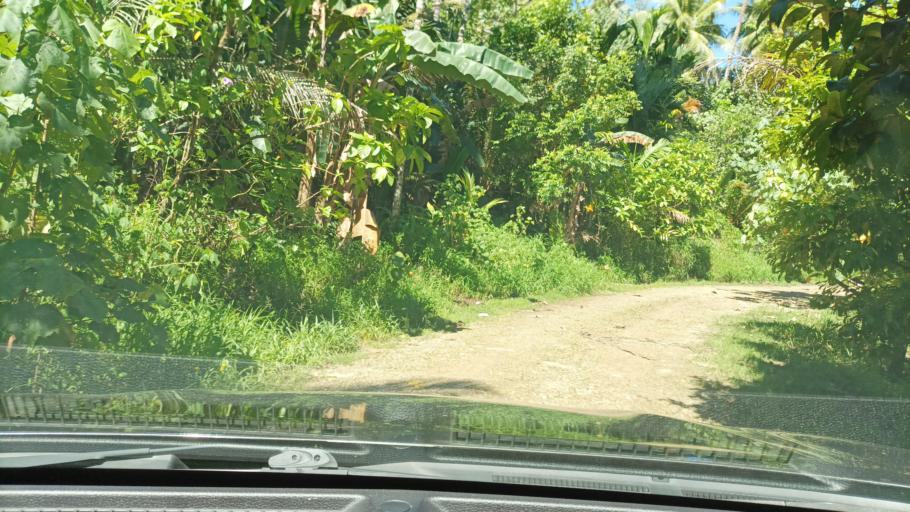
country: FM
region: Pohnpei
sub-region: Madolenihm Municipality
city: Madolenihm Municipality Government
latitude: 6.8435
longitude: 158.3193
